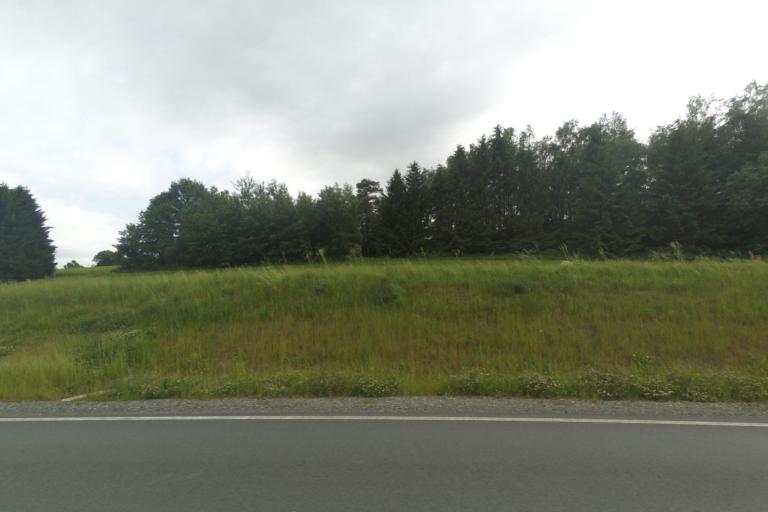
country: DE
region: Bavaria
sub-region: Upper Franconia
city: Munchberg
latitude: 50.1759
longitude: 11.8006
